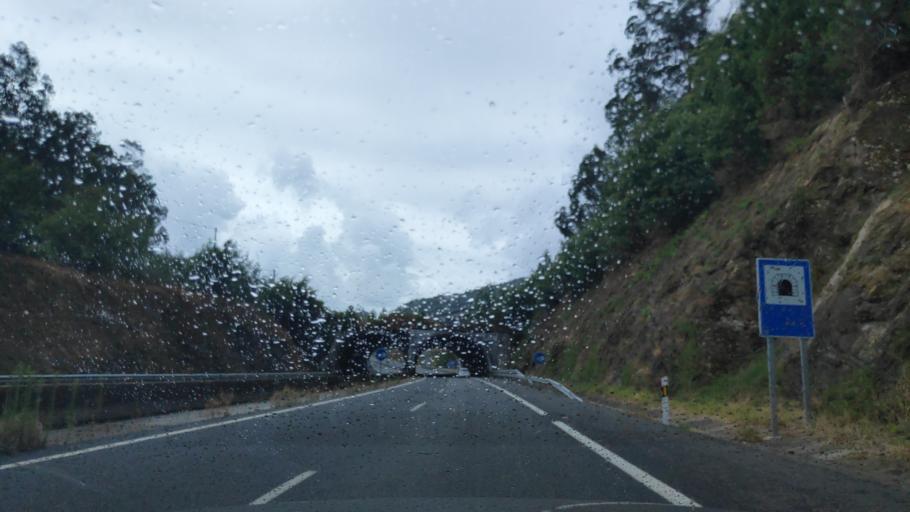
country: ES
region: Galicia
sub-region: Provincia da Coruna
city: Rois
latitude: 42.7175
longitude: -8.7256
